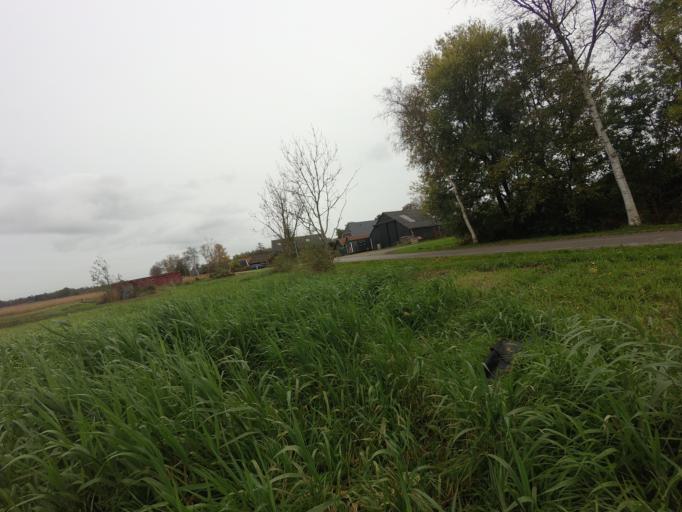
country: NL
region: Overijssel
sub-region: Gemeente Steenwijkerland
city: Blokzijl
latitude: 52.7743
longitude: 5.9608
